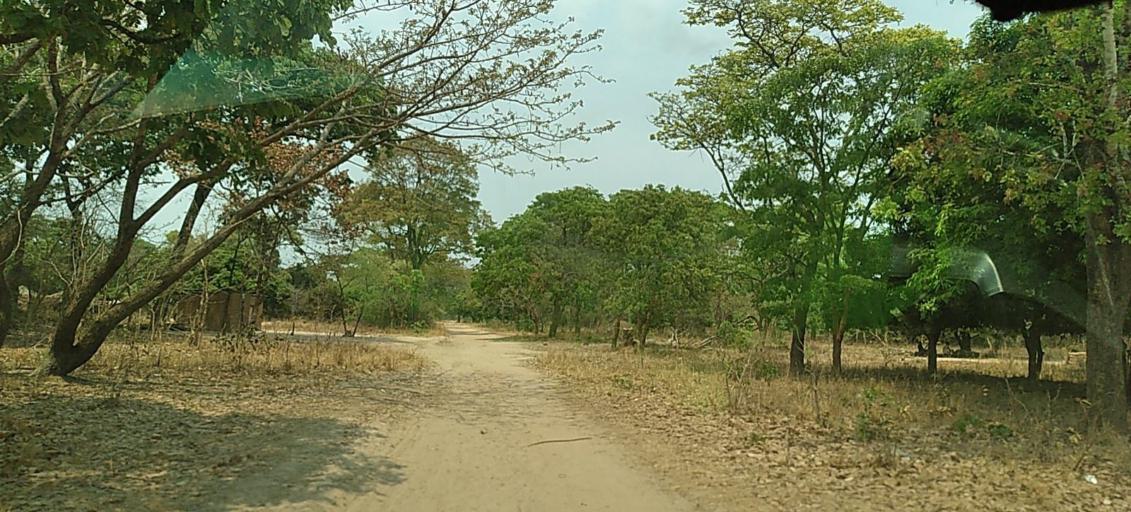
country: ZM
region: North-Western
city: Kabompo
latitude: -13.5593
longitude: 24.4464
